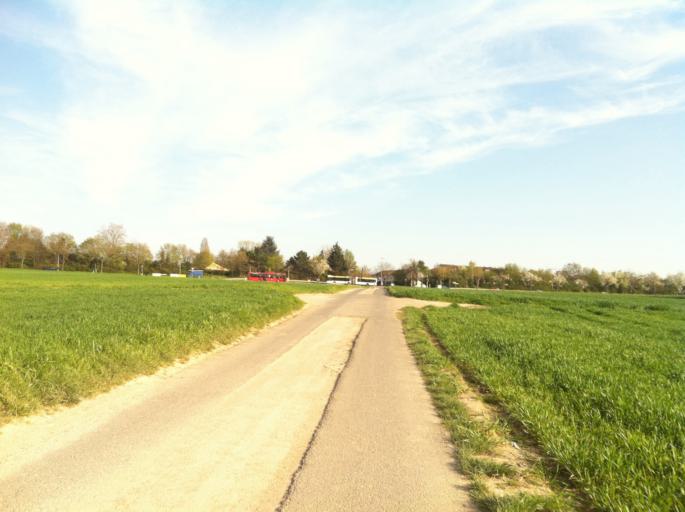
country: DE
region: Rheinland-Pfalz
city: Klein-Winternheim
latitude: 49.9746
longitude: 8.2302
